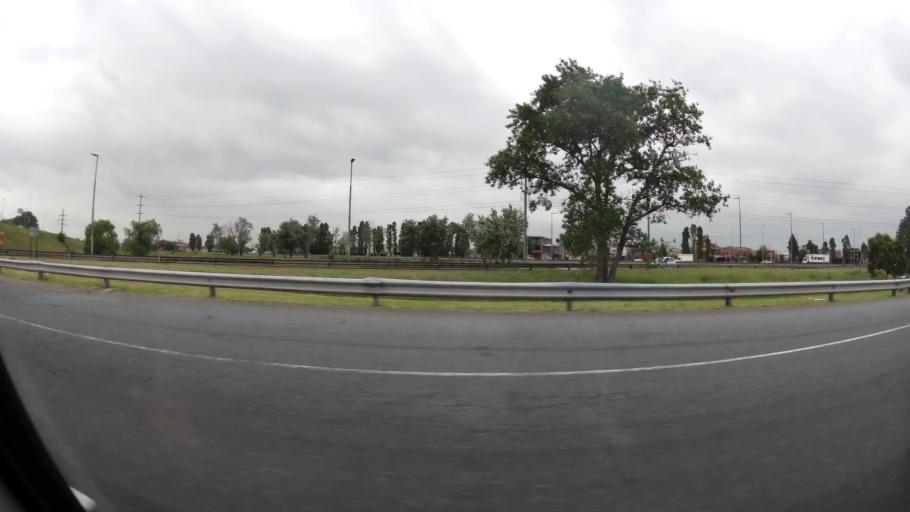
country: AR
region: Buenos Aires
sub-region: Partido de Avellaneda
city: Avellaneda
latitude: -34.6788
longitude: -58.3248
